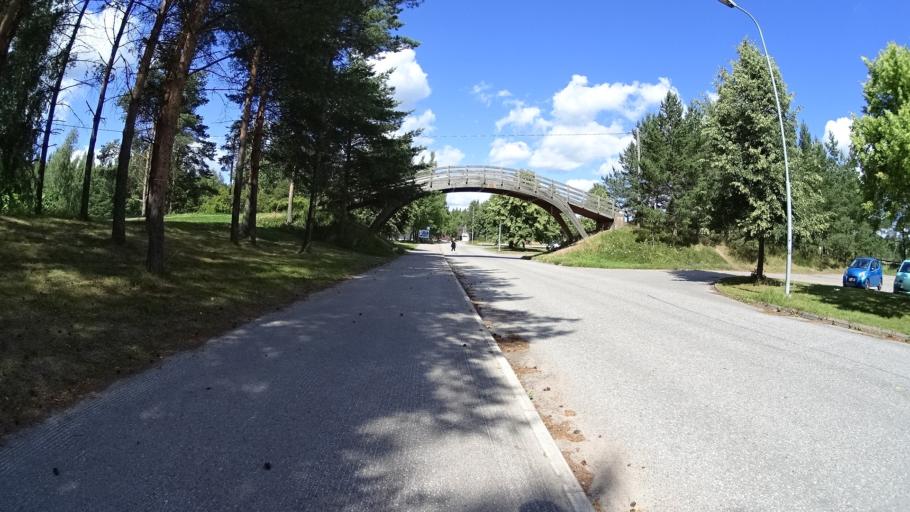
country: FI
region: Uusimaa
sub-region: Helsinki
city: Tuusula
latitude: 60.3915
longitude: 25.0304
